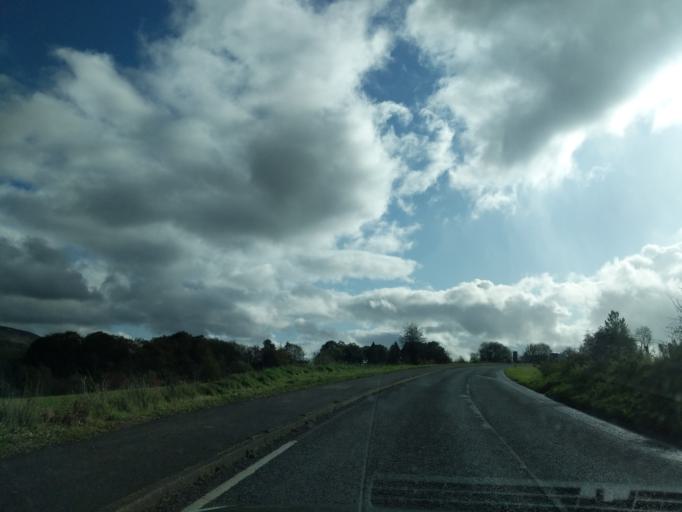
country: GB
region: Scotland
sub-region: Dumfries and Galloway
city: Moffat
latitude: 55.3214
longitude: -3.4454
